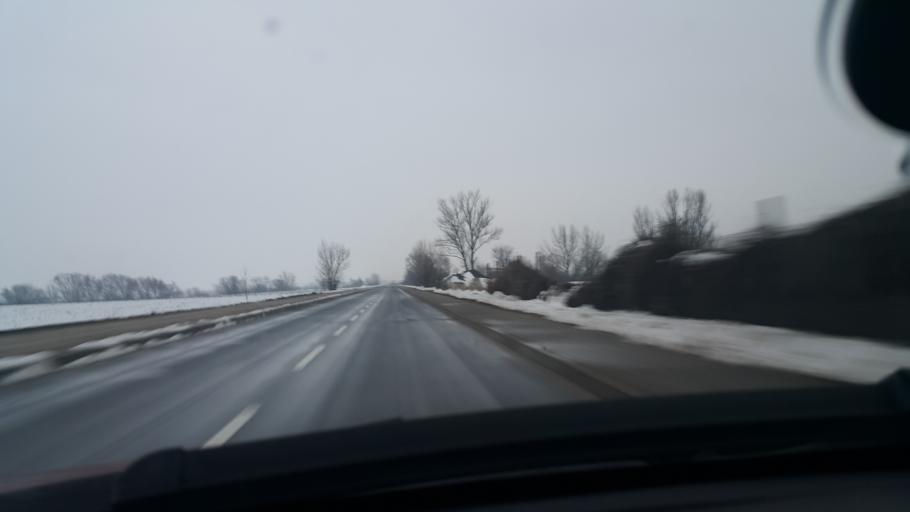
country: SI
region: Hoce-Slivnica
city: Rogoza
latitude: 46.4931
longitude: 15.6714
